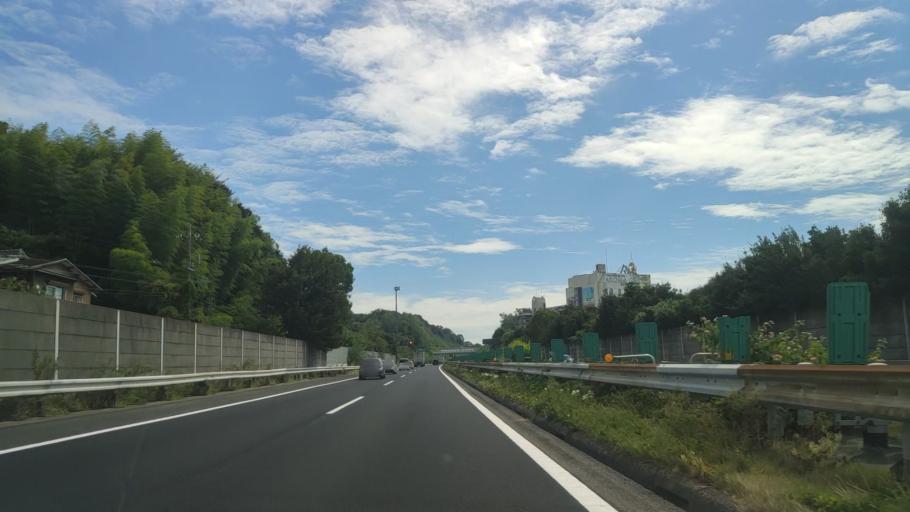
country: JP
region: Aichi
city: Okazaki
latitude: 34.9617
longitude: 137.1903
